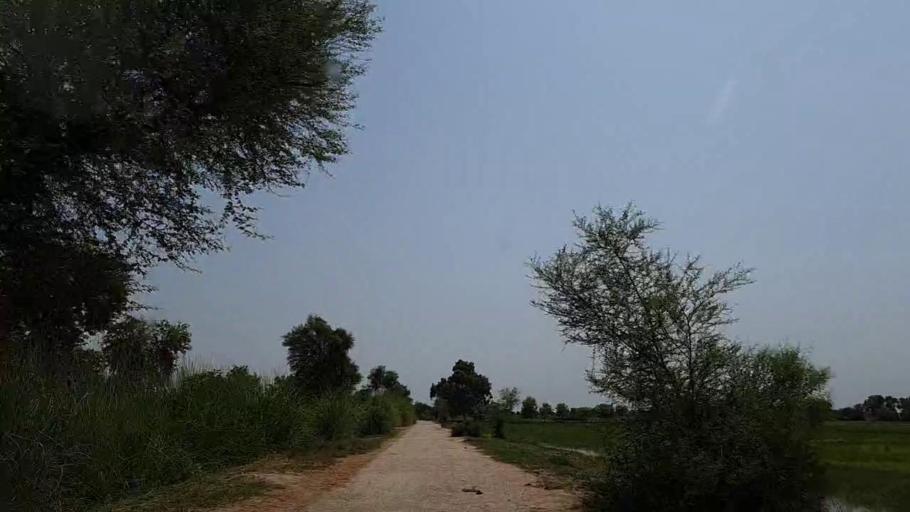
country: PK
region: Sindh
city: Adilpur
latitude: 27.9206
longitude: 69.3739
